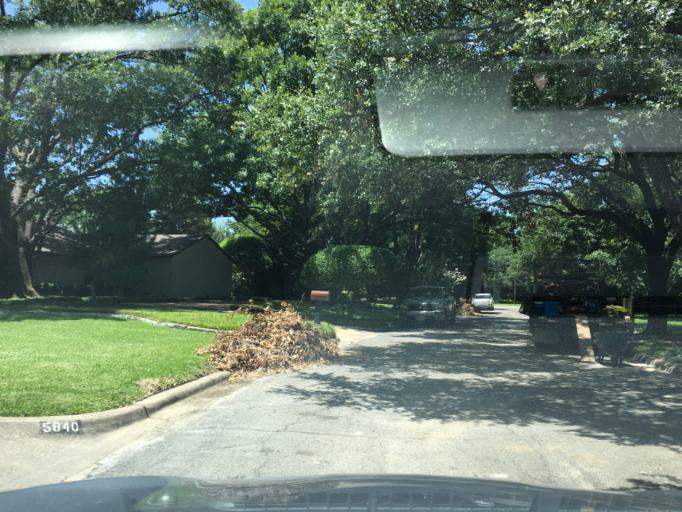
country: US
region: Texas
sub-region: Dallas County
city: University Park
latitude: 32.8819
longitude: -96.8076
